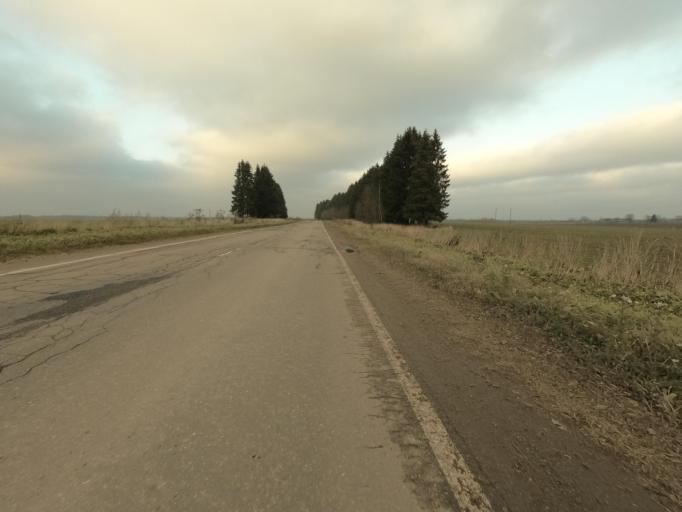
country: RU
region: Leningrad
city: Mga
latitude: 59.7778
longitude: 31.0245
